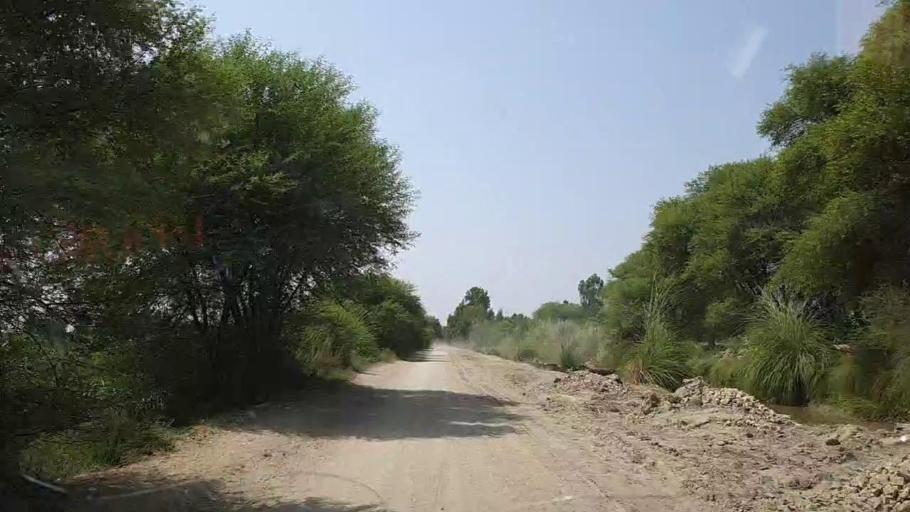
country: PK
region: Sindh
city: Ghotki
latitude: 28.0868
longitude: 69.3374
